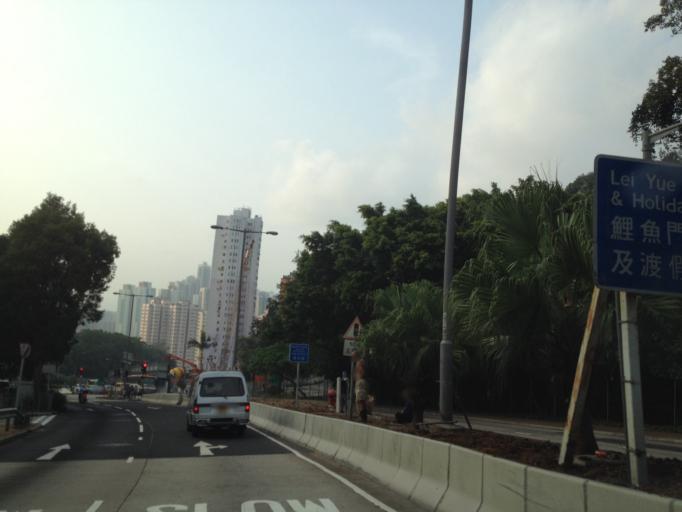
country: HK
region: Wanchai
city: Wan Chai
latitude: 22.2729
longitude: 114.2325
